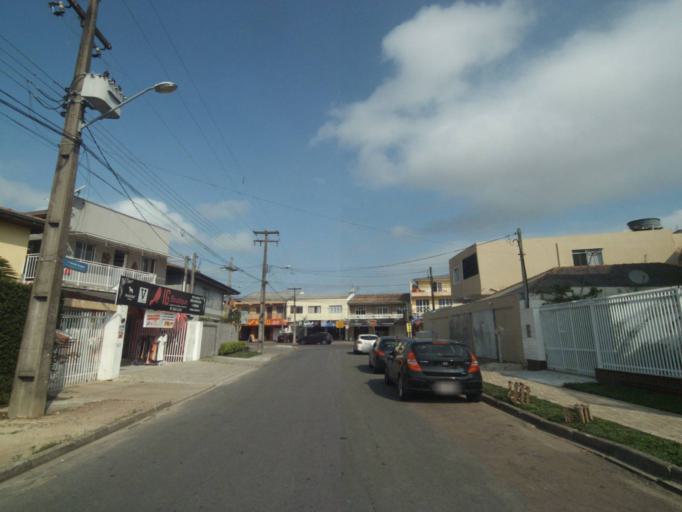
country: BR
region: Parana
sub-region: Sao Jose Dos Pinhais
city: Sao Jose dos Pinhais
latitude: -25.5393
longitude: -49.2565
